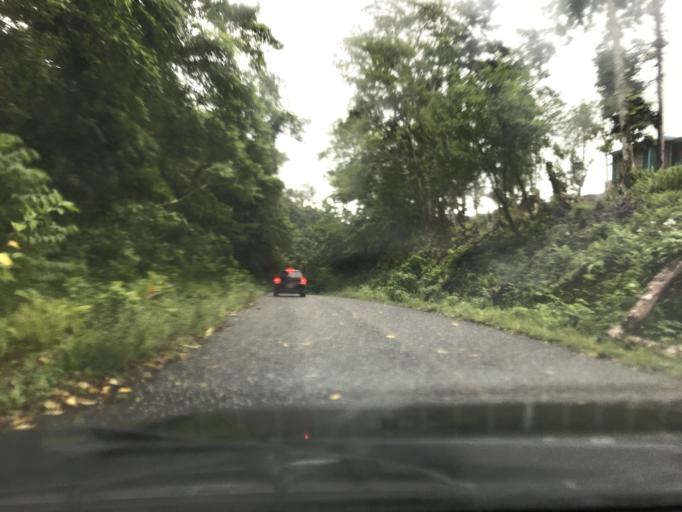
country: SB
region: Western Province
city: Gizo
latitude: -8.2874
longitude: 157.2507
